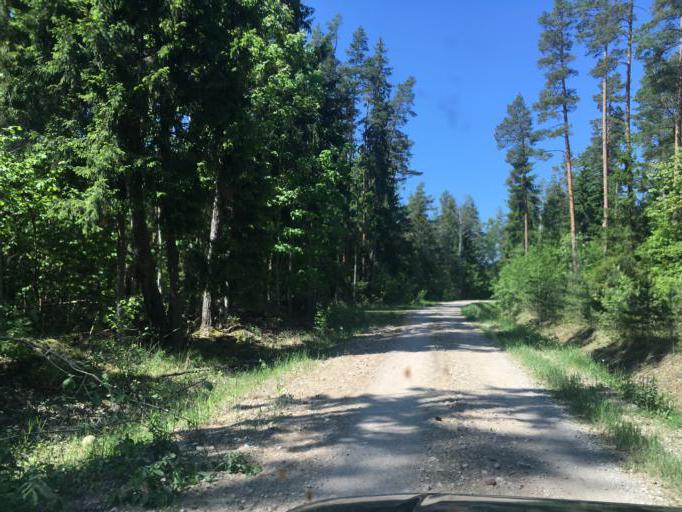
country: LV
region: Talsu Rajons
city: Valdemarpils
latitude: 57.4465
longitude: 22.6561
